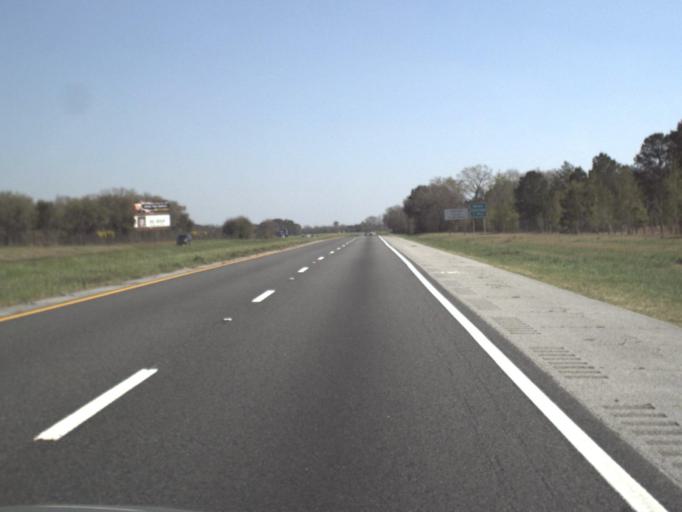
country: US
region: Florida
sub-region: Jackson County
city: Sneads
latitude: 30.6479
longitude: -85.0121
